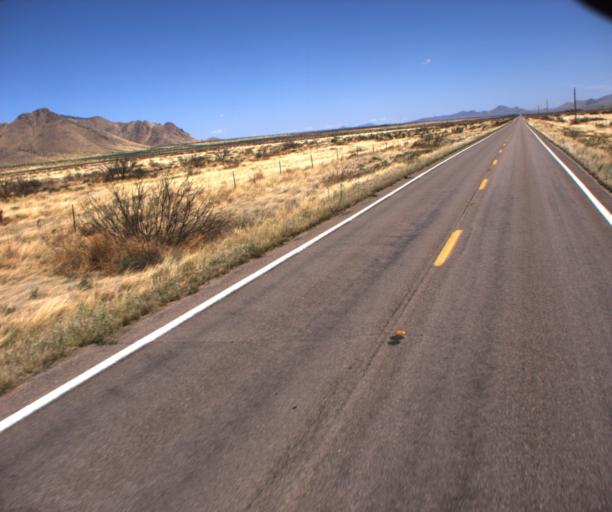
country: US
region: Arizona
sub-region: Cochise County
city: Douglas
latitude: 31.7118
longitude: -109.1180
